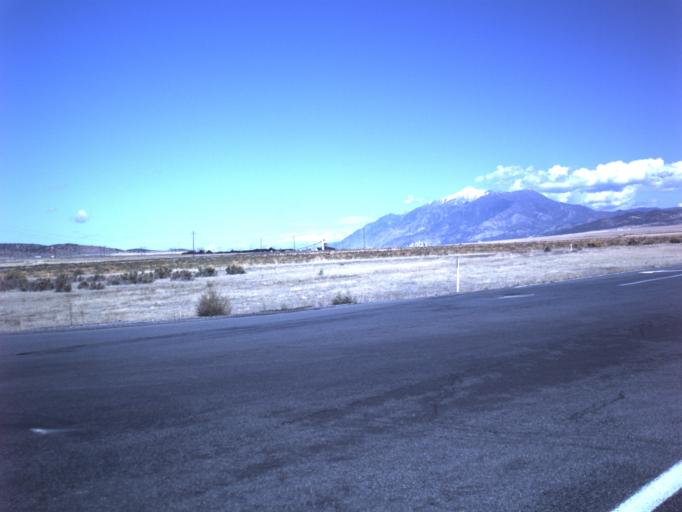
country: US
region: Utah
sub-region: Juab County
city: Nephi
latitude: 39.5567
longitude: -111.9189
